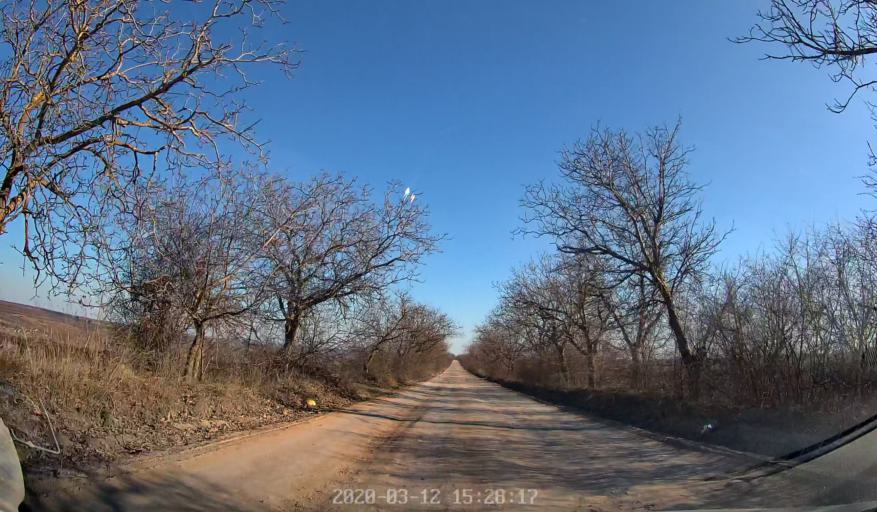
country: MD
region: Chisinau
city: Ciorescu
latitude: 47.1695
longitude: 28.9301
